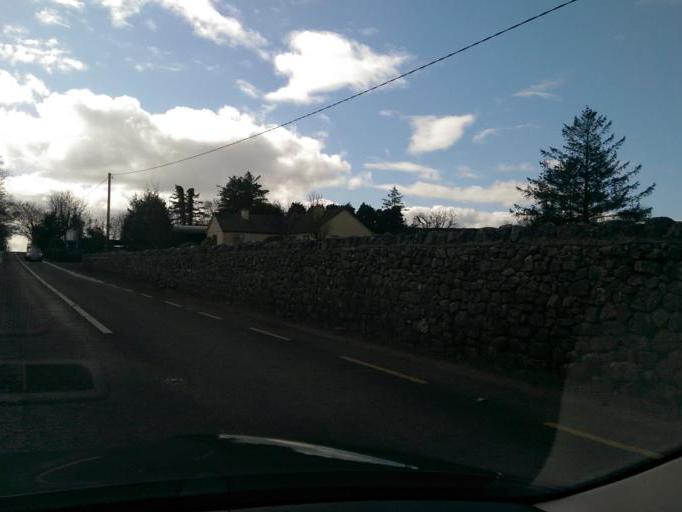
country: IE
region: Connaught
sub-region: County Galway
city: Athenry
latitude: 53.3715
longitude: -8.7099
